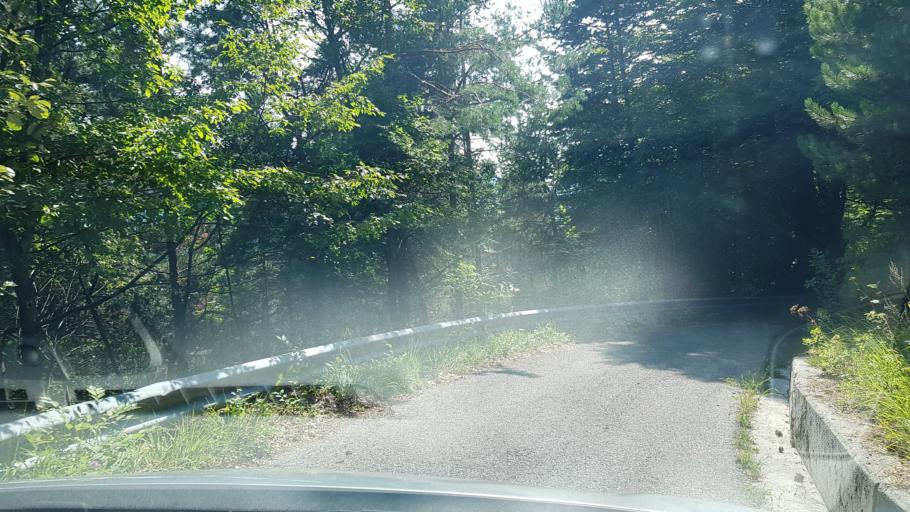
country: IT
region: Friuli Venezia Giulia
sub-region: Provincia di Udine
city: Moggio Udinese
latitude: 46.4455
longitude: 13.2154
